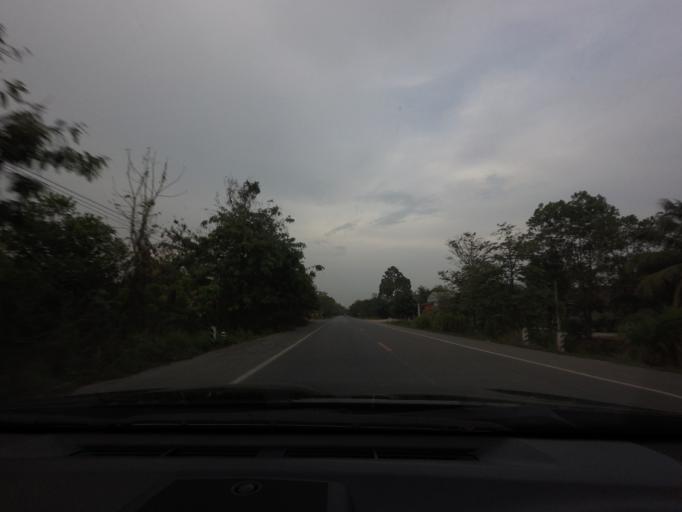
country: TH
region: Surat Thani
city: Phunphin
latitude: 9.1500
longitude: 99.1529
